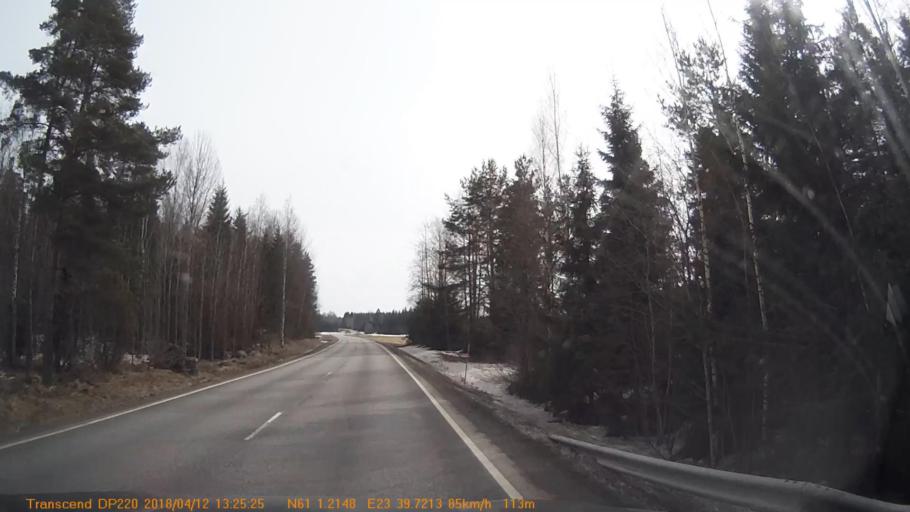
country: FI
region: Pirkanmaa
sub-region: Etelae-Pirkanmaa
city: Kylmaekoski
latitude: 61.0200
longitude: 23.6623
